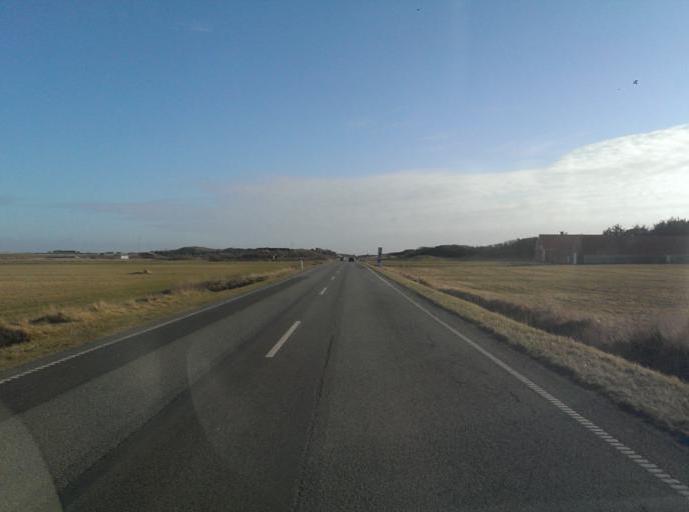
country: DK
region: Central Jutland
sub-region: Ringkobing-Skjern Kommune
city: Hvide Sande
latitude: 55.9648
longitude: 8.1456
